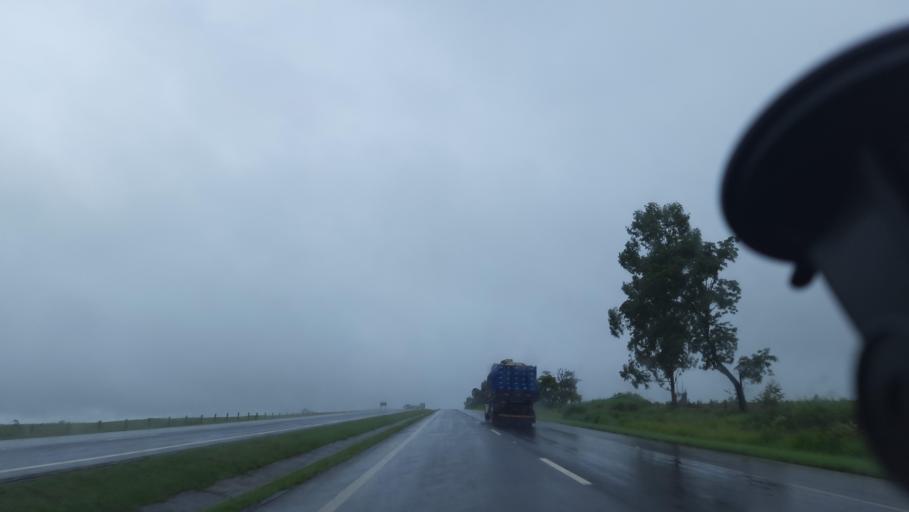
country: BR
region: Sao Paulo
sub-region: Aguai
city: Aguai
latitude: -22.0188
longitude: -47.0349
